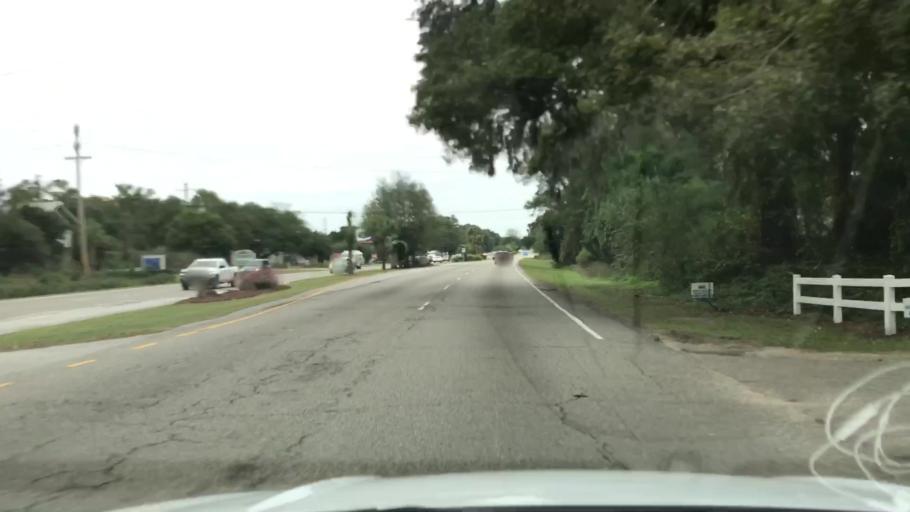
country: US
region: South Carolina
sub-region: Georgetown County
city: Murrells Inlet
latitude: 33.4778
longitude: -79.1009
